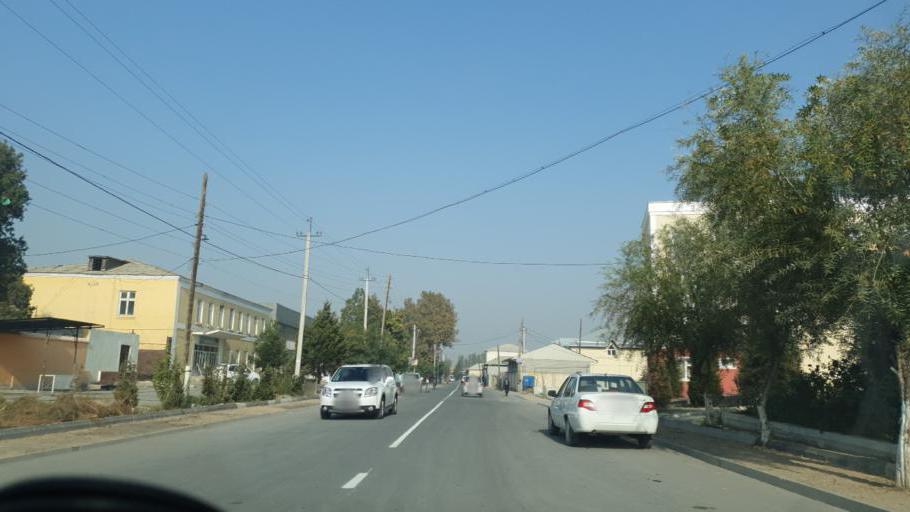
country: UZ
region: Fergana
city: Qo`qon
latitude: 40.5790
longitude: 70.9142
